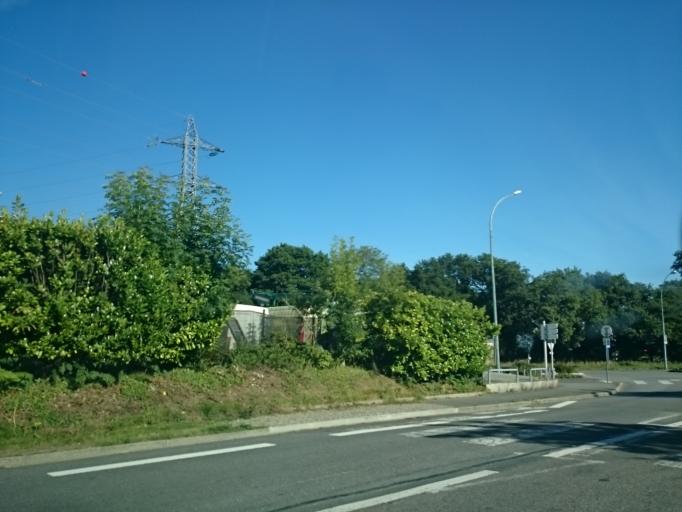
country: FR
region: Brittany
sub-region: Departement du Finistere
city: Gouesnou
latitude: 48.4249
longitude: -4.4604
